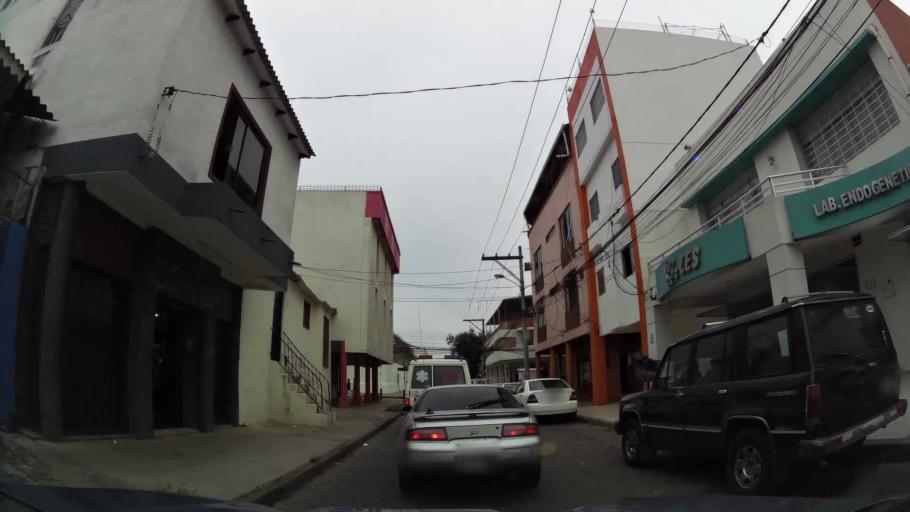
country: BO
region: Santa Cruz
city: Santa Cruz de la Sierra
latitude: -17.7801
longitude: -63.1874
